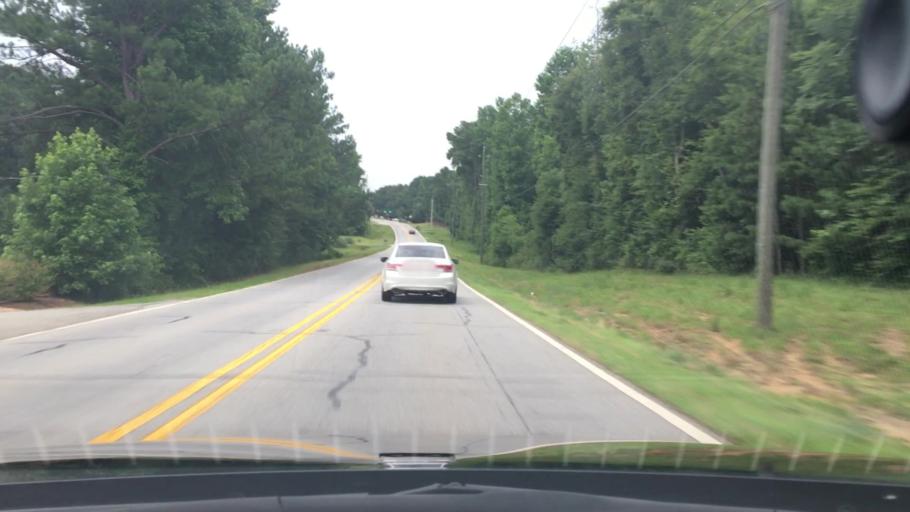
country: US
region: Georgia
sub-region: Coweta County
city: East Newnan
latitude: 33.3553
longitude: -84.7071
